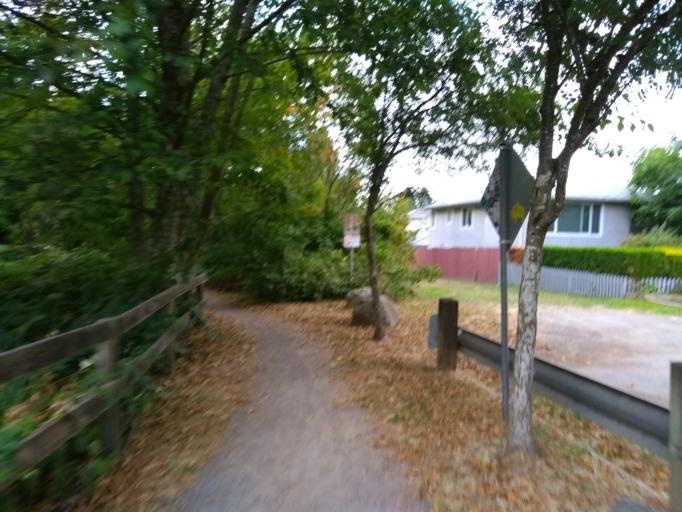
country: CA
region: British Columbia
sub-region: Fraser Valley Regional District
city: North Vancouver
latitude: 49.2470
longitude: -123.0432
